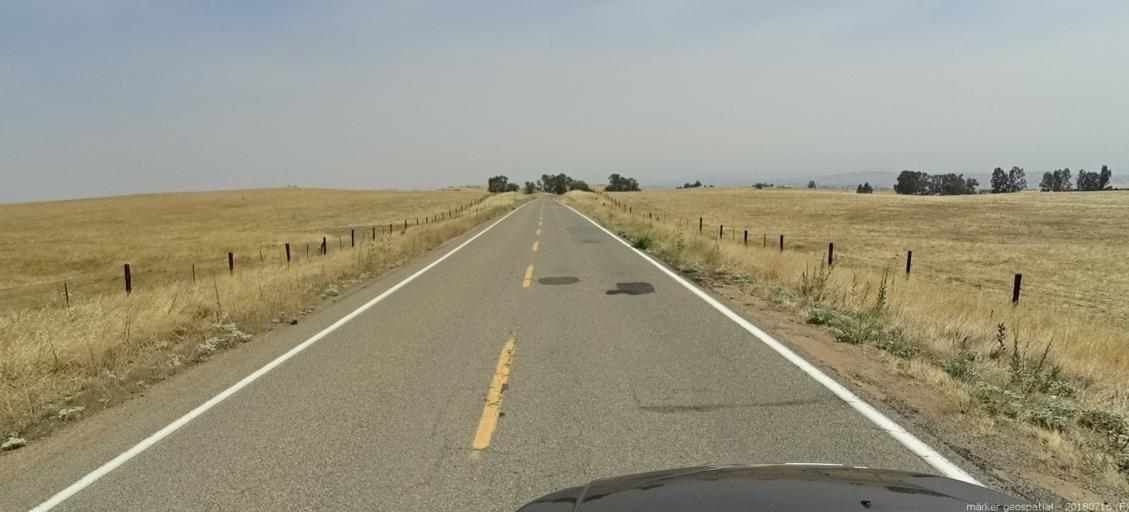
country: US
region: California
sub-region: Madera County
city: Bonadelle Ranchos-Madera Ranchos
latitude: 37.0994
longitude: -119.9442
